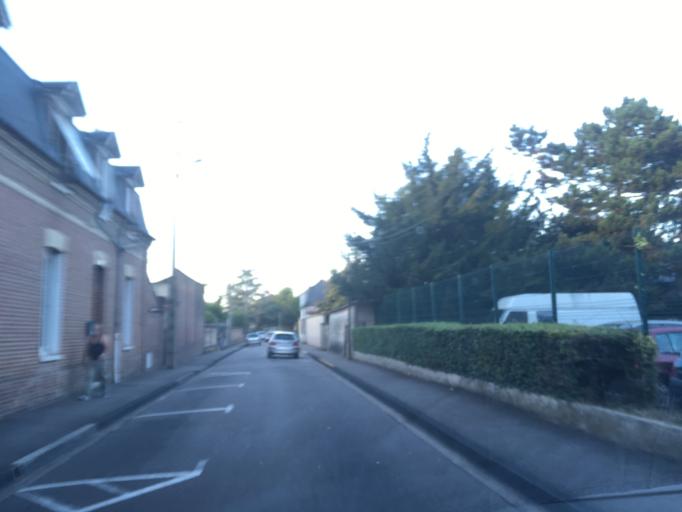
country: FR
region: Haute-Normandie
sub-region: Departement de l'Eure
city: Gaillon
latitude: 49.1610
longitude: 1.3369
